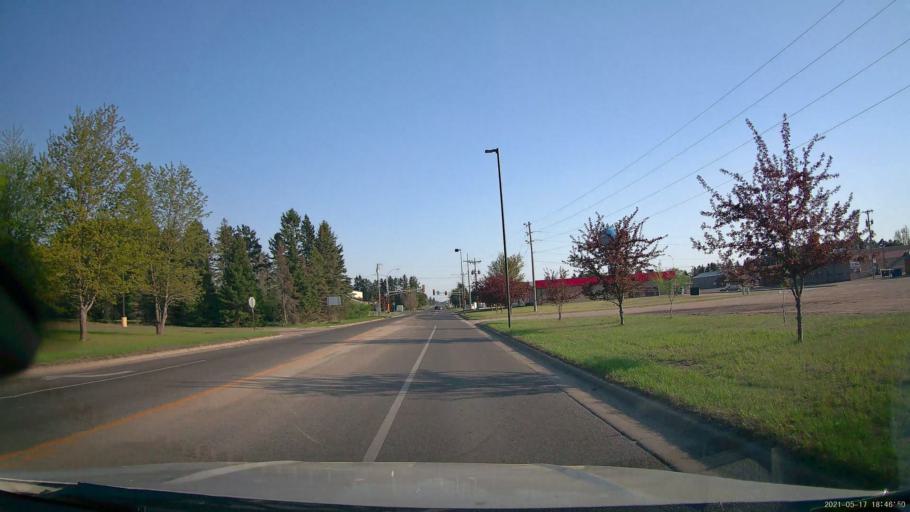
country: US
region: Minnesota
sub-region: Hubbard County
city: Park Rapids
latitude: 46.9232
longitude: -95.0371
